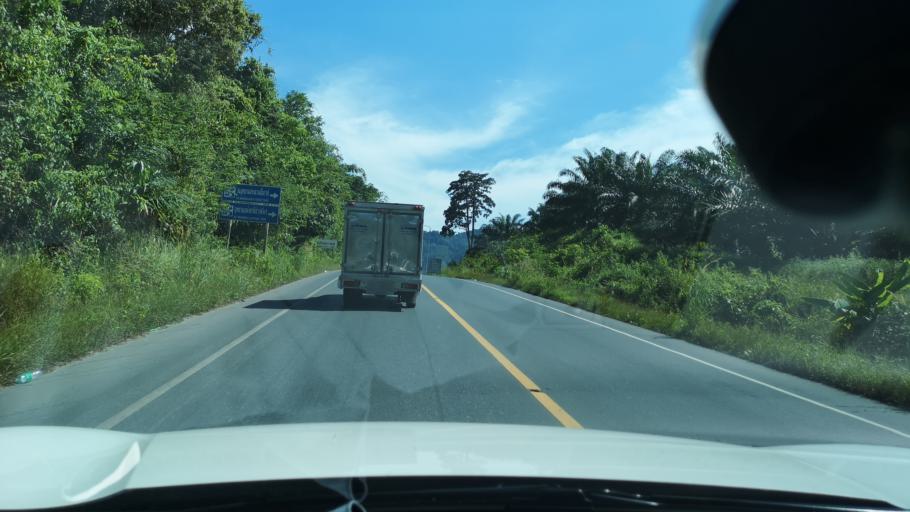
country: TH
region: Phangnga
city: Phang Nga
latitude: 8.5275
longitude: 98.5183
